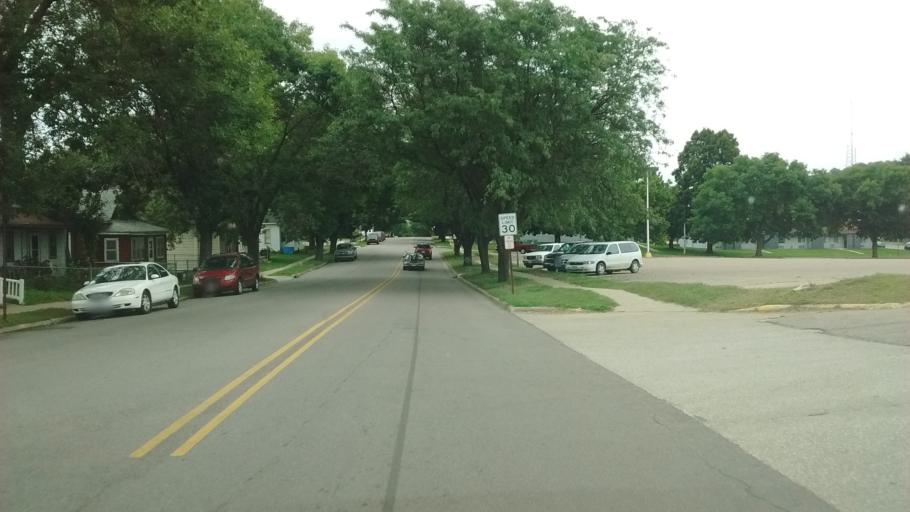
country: US
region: Iowa
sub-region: Woodbury County
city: Sioux City
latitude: 42.4998
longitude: -96.4196
